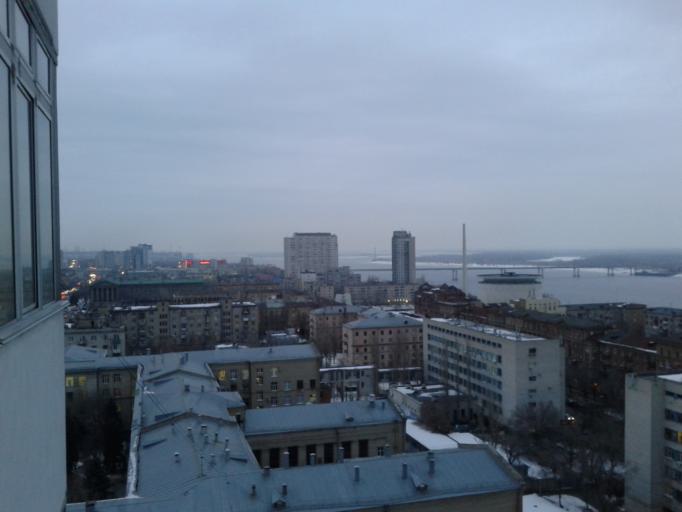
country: RU
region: Volgograd
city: Volgograd
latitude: 48.7129
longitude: 44.5275
